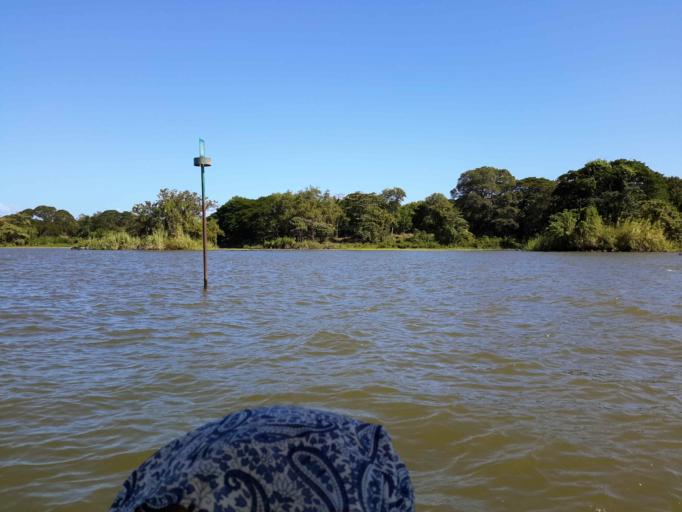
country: NI
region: Granada
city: Granada
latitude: 11.9151
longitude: -85.9269
